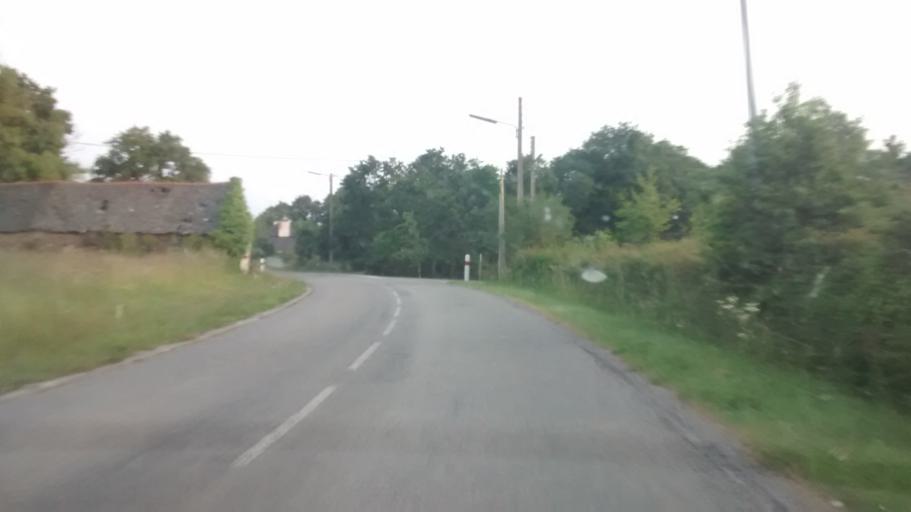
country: FR
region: Brittany
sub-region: Departement du Morbihan
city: Beignon
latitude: 47.9701
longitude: -2.1518
